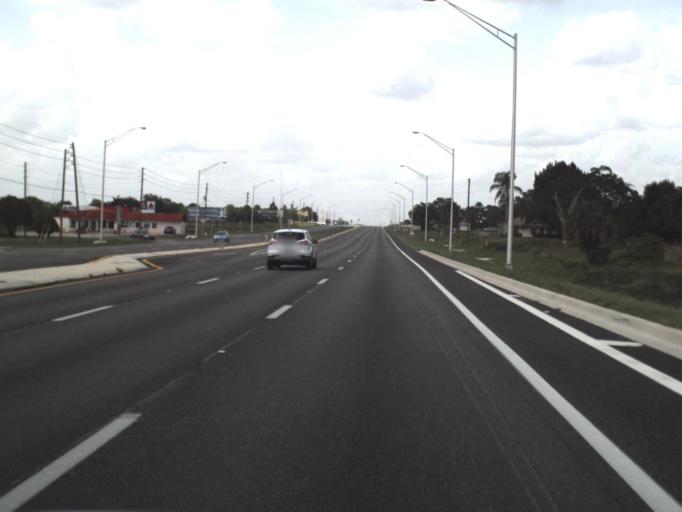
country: US
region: Florida
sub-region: Highlands County
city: Avon Park
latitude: 27.6332
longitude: -81.5177
